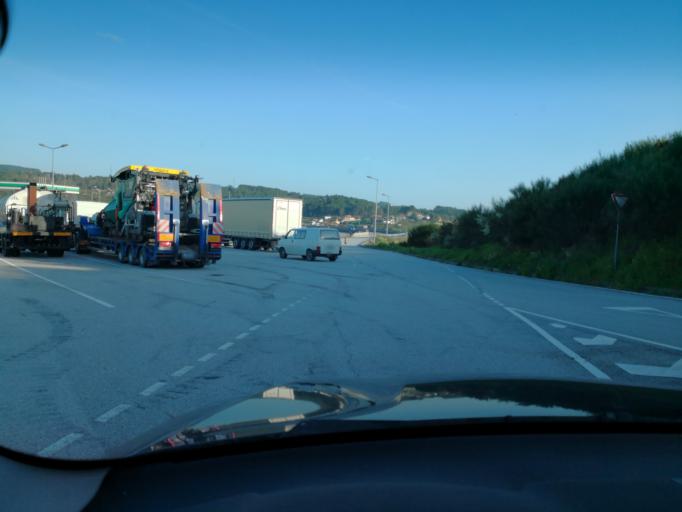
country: PT
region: Vila Real
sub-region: Vila Real
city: Vila Real
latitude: 41.3378
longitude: -7.7059
